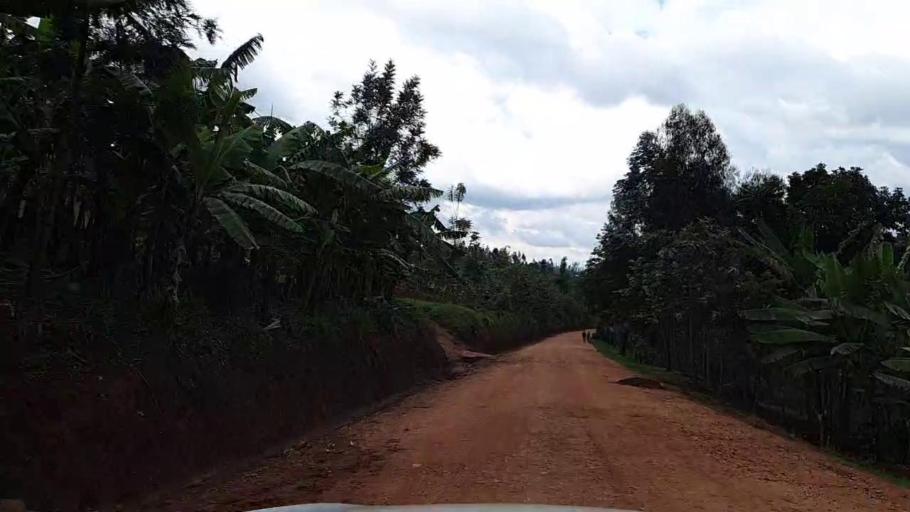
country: RW
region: Southern Province
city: Nyanza
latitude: -2.4134
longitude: 29.6716
